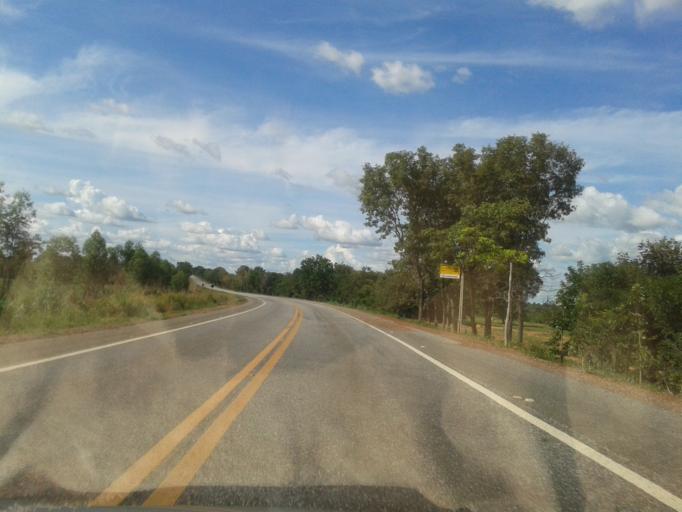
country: BR
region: Goias
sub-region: Mozarlandia
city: Mozarlandia
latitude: -14.8963
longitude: -50.5487
